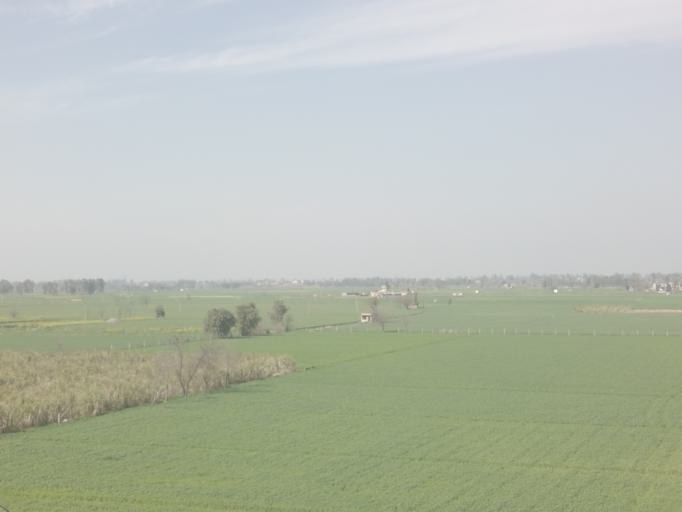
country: IN
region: Punjab
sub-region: Shahid Bhagat Singh Nagar
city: Rahon
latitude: 31.0231
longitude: 76.0925
